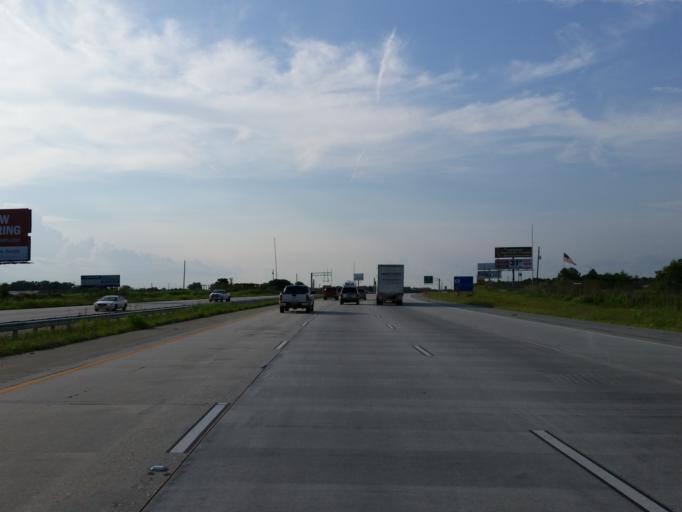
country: US
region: Georgia
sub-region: Dooly County
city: Unadilla
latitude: 32.2543
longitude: -83.7473
